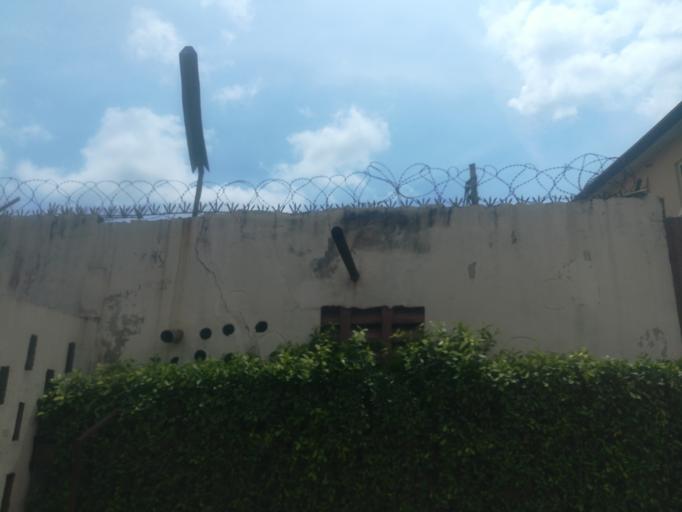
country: NG
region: Lagos
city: Ojota
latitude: 6.5605
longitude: 3.3856
